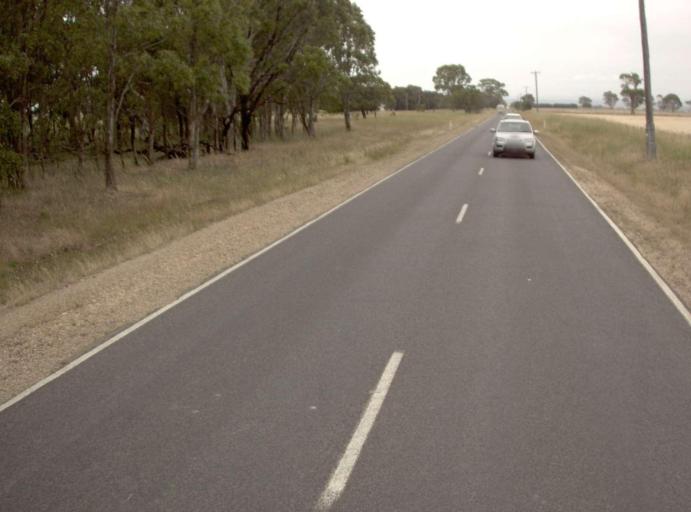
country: AU
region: Victoria
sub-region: Wellington
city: Heyfield
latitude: -38.0489
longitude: 146.7679
